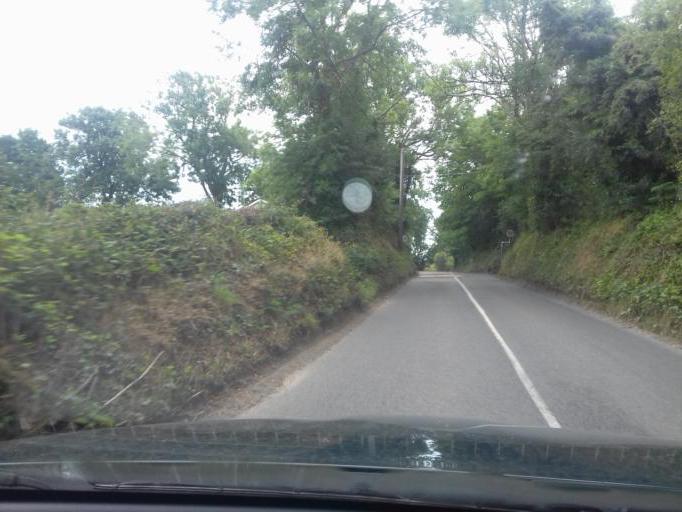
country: IE
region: Leinster
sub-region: Loch Garman
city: Castlebridge
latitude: 52.4147
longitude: -6.4105
